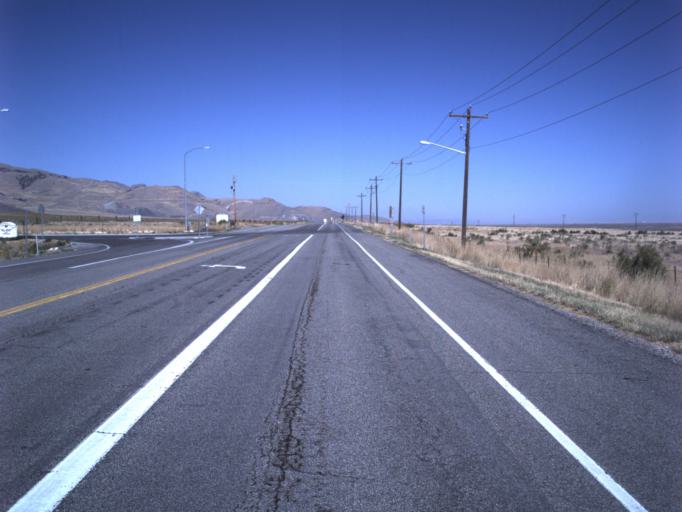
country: US
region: Utah
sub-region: Tooele County
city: Grantsville
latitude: 40.6251
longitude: -112.5076
